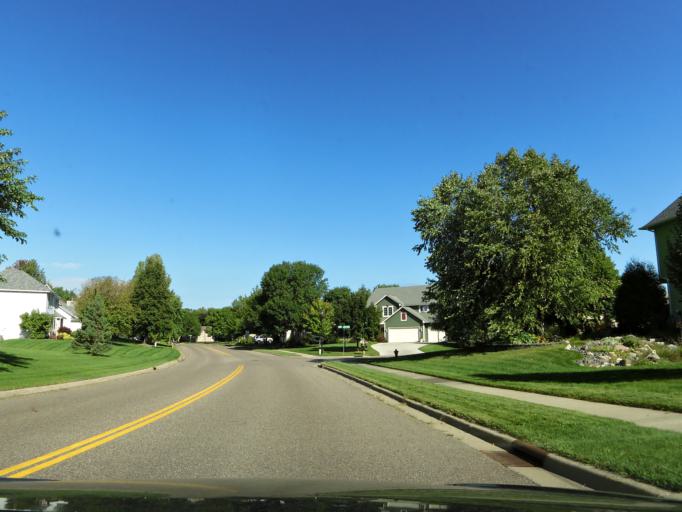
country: US
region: Minnesota
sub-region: Scott County
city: Savage
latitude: 44.7363
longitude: -93.3365
